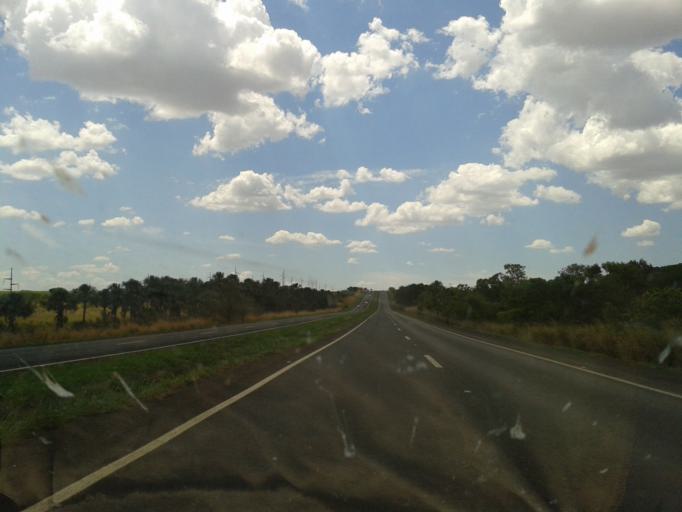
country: BR
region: Minas Gerais
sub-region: Uberlandia
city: Uberlandia
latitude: -19.1107
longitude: -48.1783
